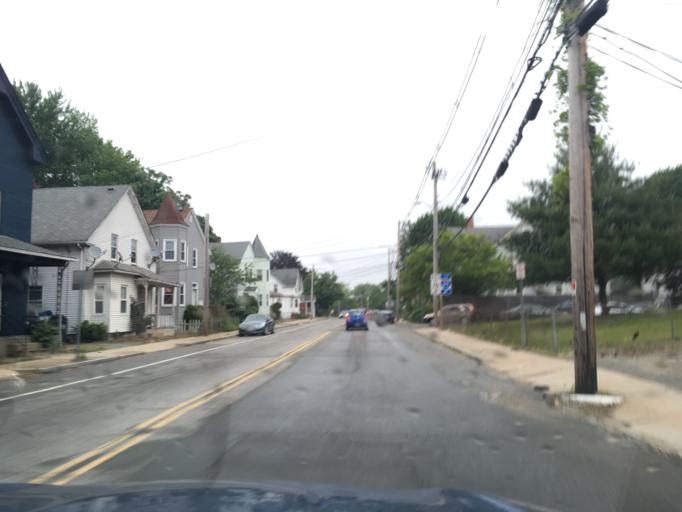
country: US
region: Rhode Island
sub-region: Providence County
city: Cranston
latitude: 41.7762
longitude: -71.4213
